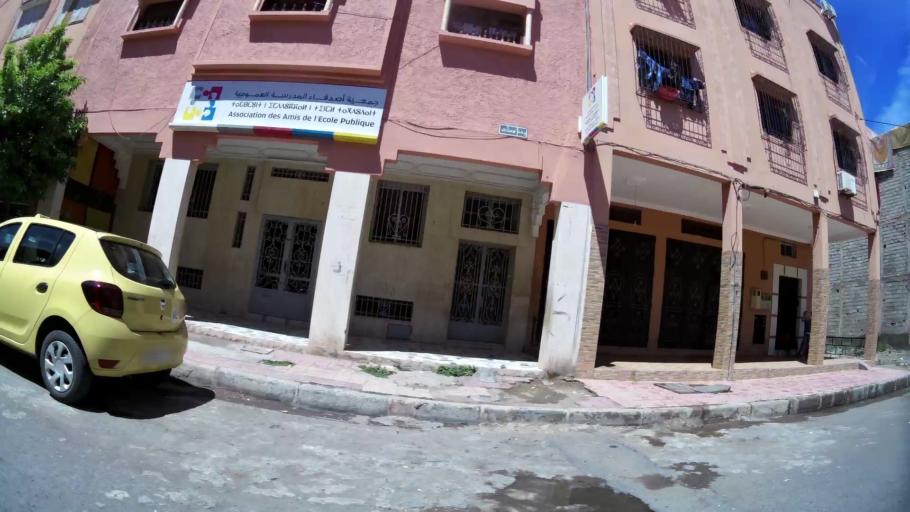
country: MA
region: Marrakech-Tensift-Al Haouz
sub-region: Marrakech
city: Marrakesh
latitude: 31.6402
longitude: -8.0661
